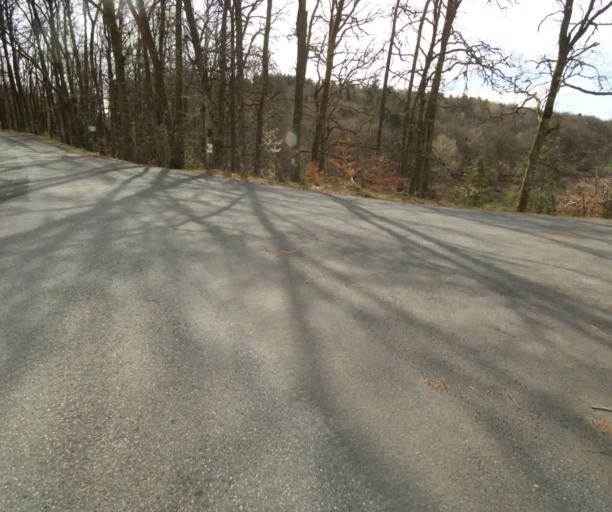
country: FR
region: Limousin
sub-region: Departement de la Correze
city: Correze
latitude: 45.3700
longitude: 1.9163
